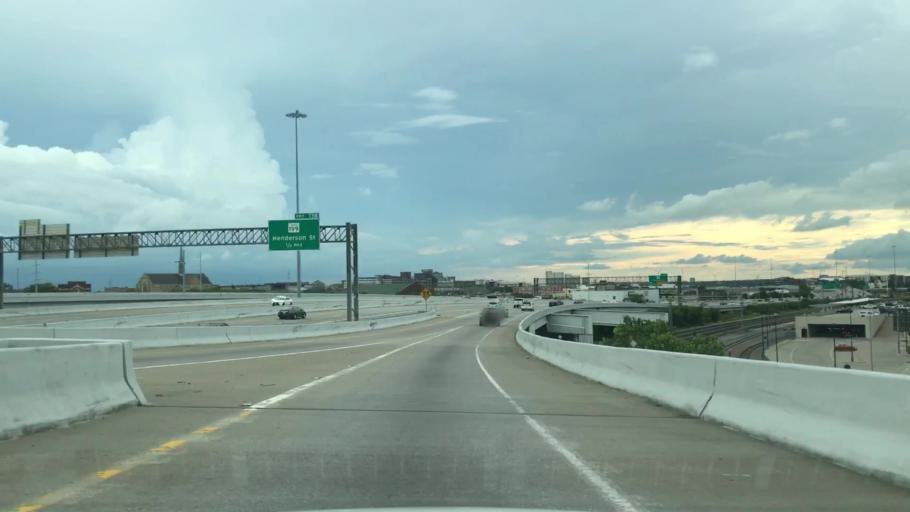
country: US
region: Texas
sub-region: Tarrant County
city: Fort Worth
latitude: 32.7456
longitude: -97.3235
